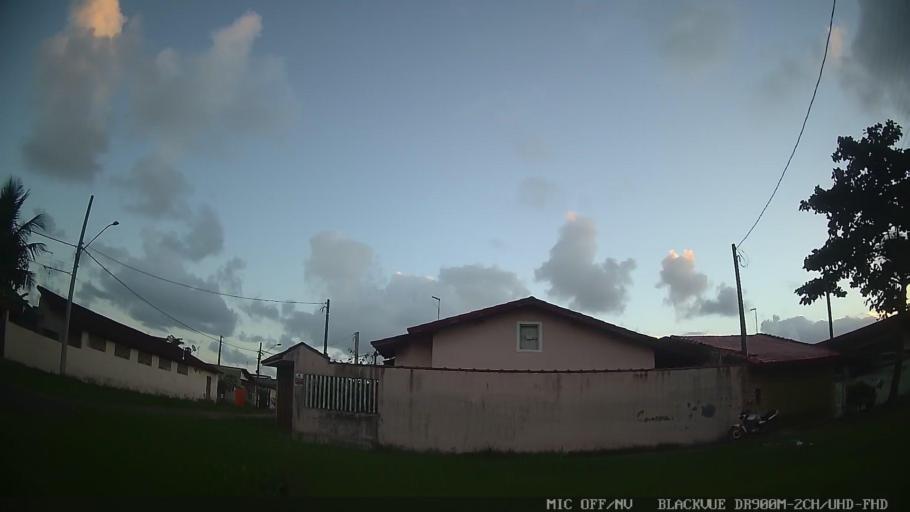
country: BR
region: Sao Paulo
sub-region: Itanhaem
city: Itanhaem
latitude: -24.1485
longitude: -46.7346
